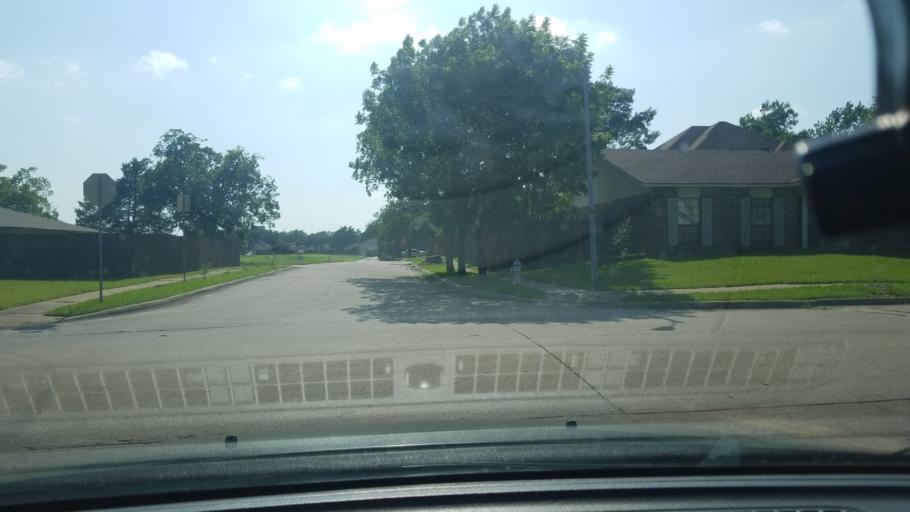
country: US
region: Texas
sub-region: Dallas County
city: Mesquite
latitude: 32.8218
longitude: -96.6149
